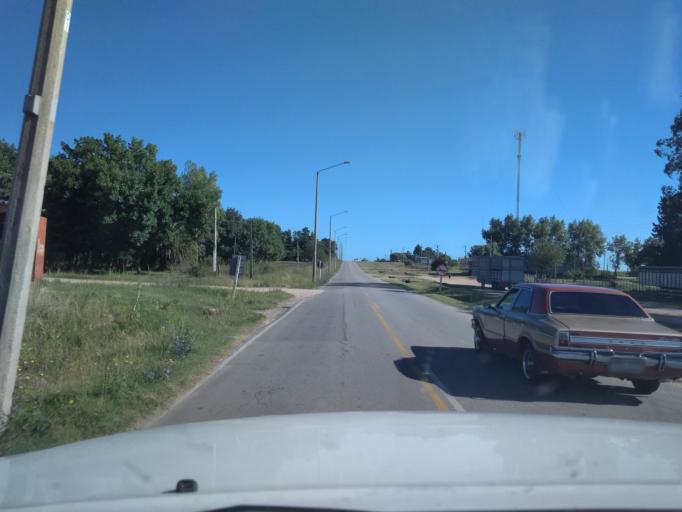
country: UY
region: Canelones
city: San Ramon
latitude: -34.3083
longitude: -55.9585
